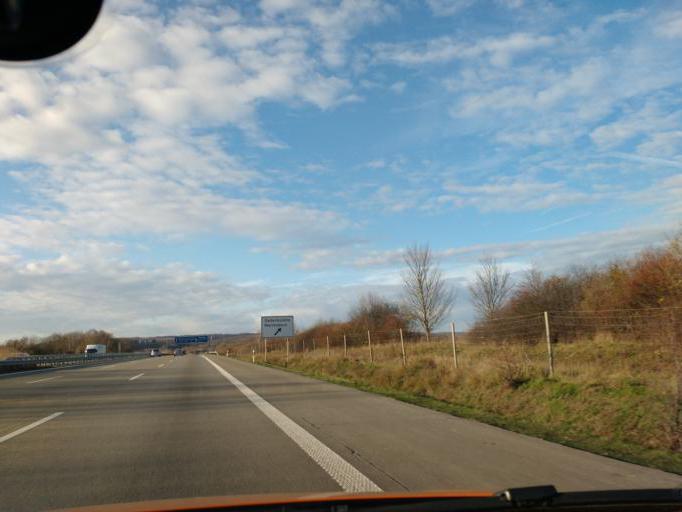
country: DE
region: Saxony-Anhalt
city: Wefensleben
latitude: 52.2082
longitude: 11.1458
